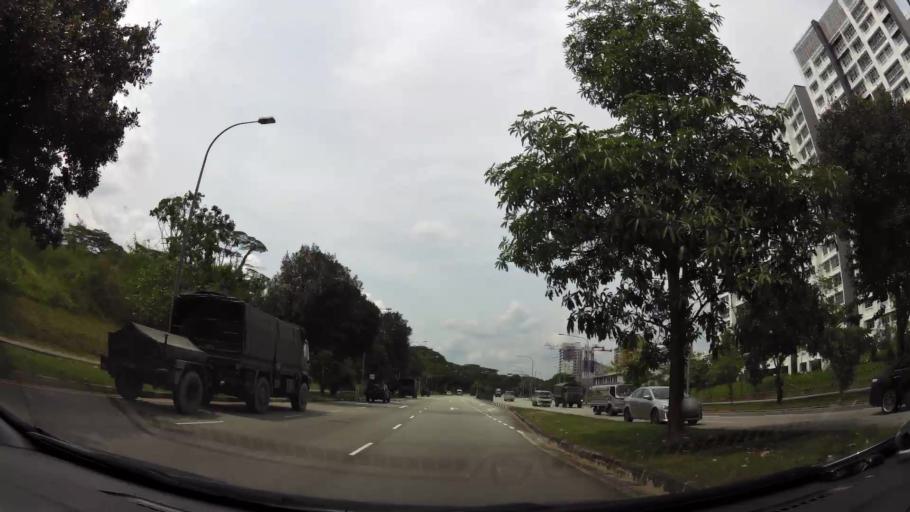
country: MY
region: Johor
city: Johor Bahru
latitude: 1.3724
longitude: 103.7423
